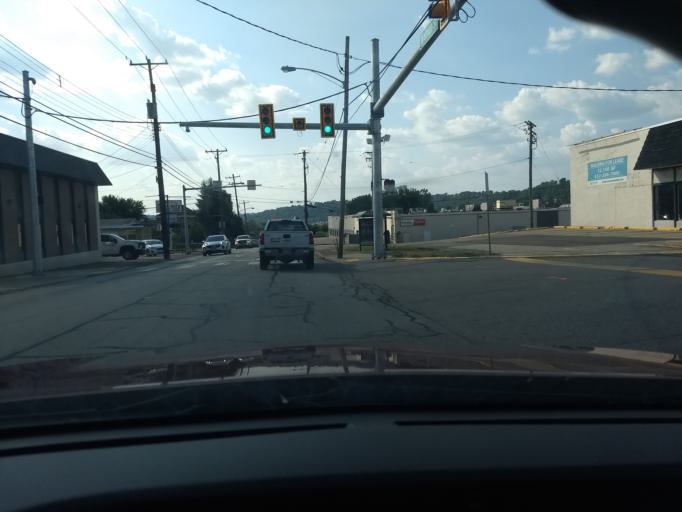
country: US
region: Pennsylvania
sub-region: Allegheny County
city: Versailles
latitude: 40.3210
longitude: -79.8365
